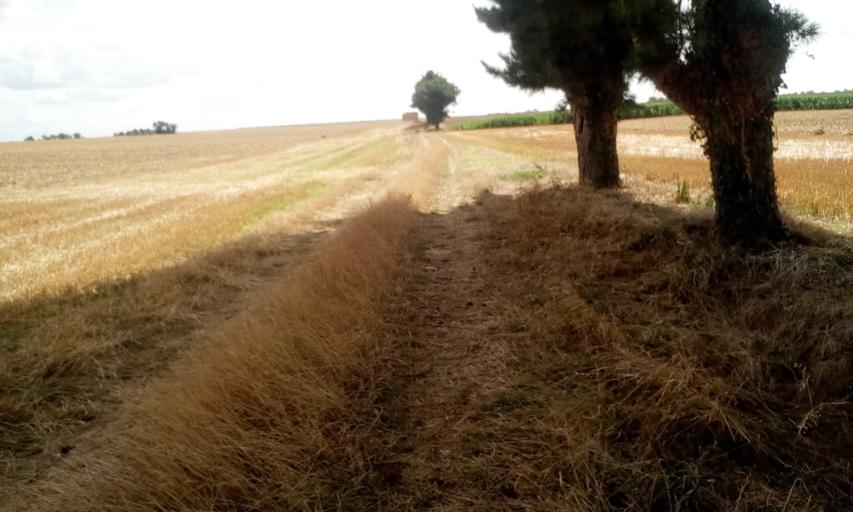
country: FR
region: Lower Normandy
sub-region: Departement du Calvados
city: Bellengreville
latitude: 49.0931
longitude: -0.2034
